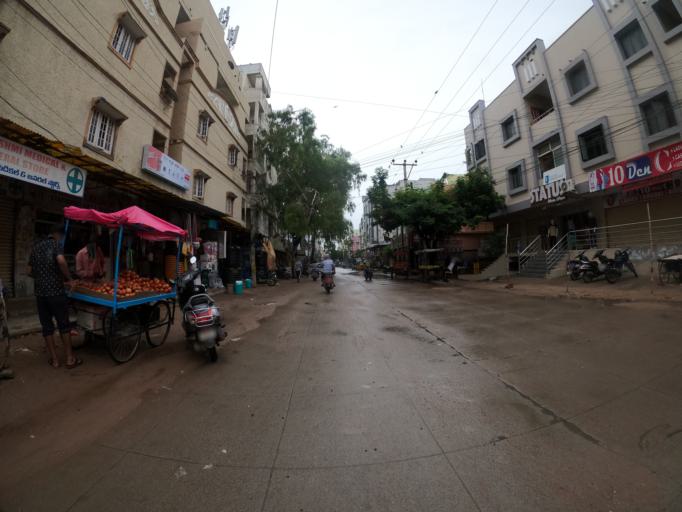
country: IN
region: Telangana
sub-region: Rangareddi
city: Kukatpalli
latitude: 17.4599
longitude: 78.3998
